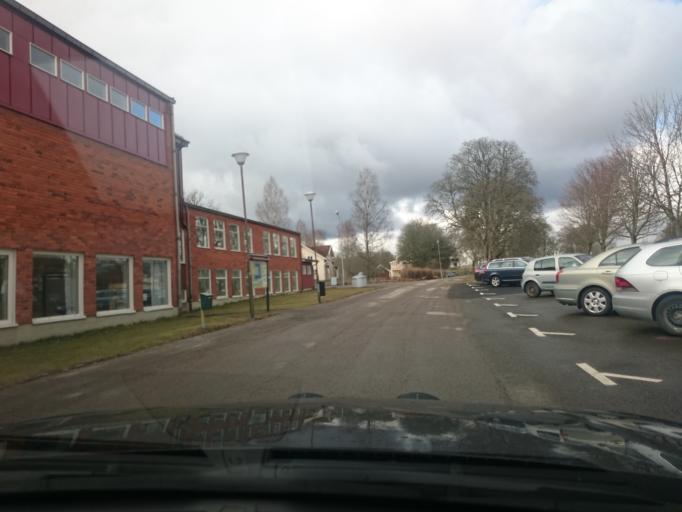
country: SE
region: Joenkoeping
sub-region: Vetlanda Kommun
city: Vetlanda
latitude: 57.3046
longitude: 15.1245
